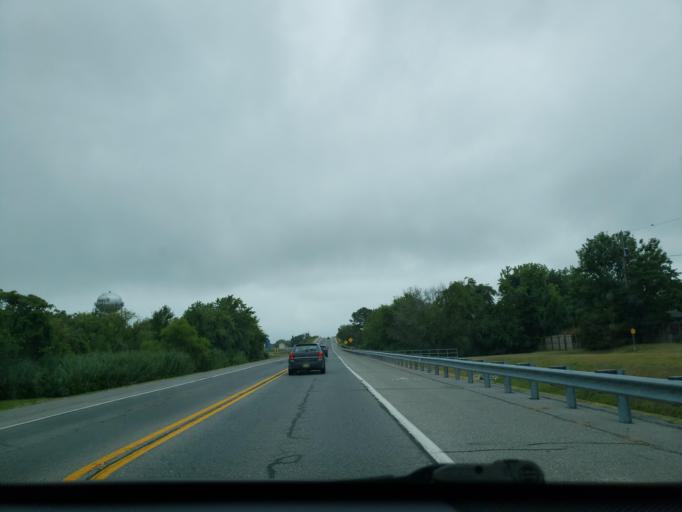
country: US
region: Delaware
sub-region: Sussex County
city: Lewes
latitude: 38.7692
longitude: -75.1375
